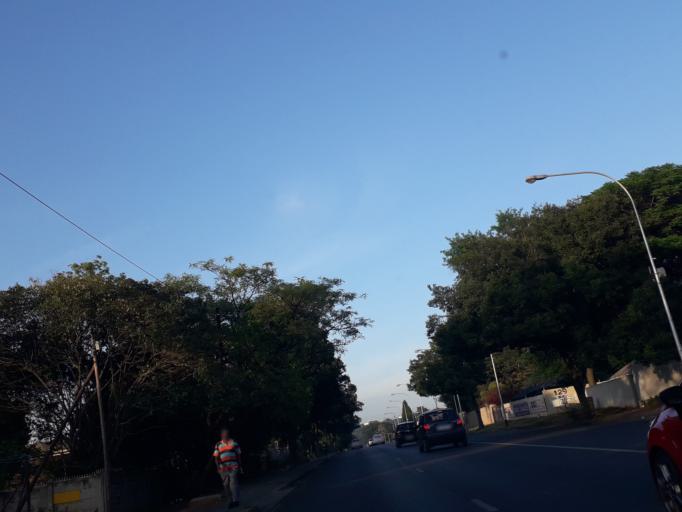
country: ZA
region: Gauteng
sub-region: City of Johannesburg Metropolitan Municipality
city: Modderfontein
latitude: -26.1270
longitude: 28.1058
